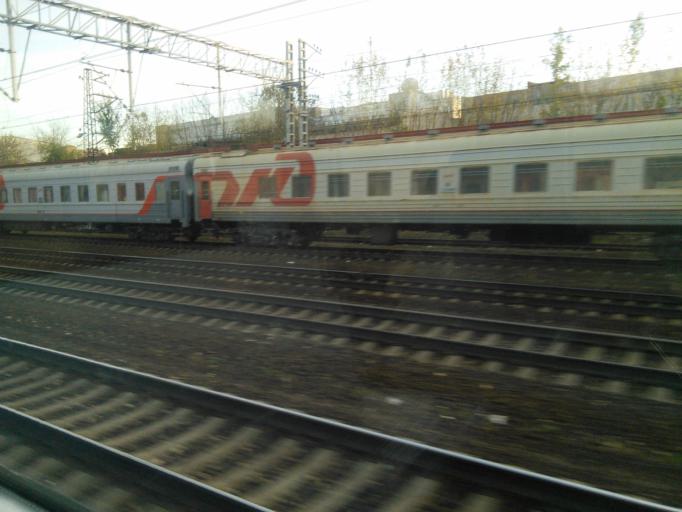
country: RU
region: Moscow
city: Khimki
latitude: 55.9003
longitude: 37.4376
